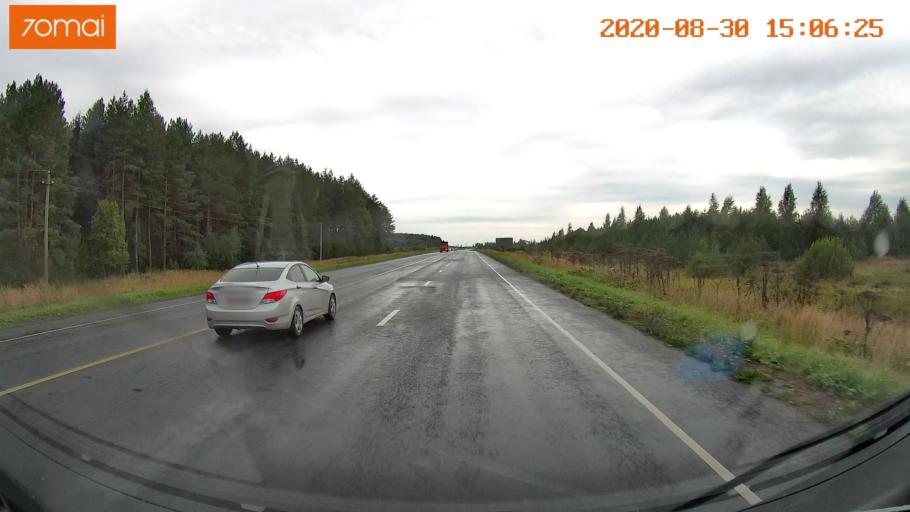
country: RU
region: Ivanovo
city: Staraya Vichuga
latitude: 57.2592
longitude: 41.9024
